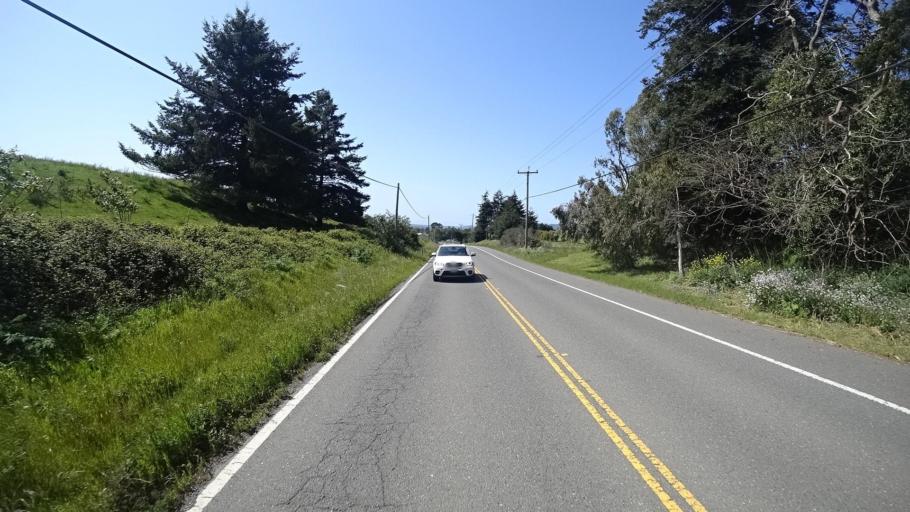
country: US
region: California
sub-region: Humboldt County
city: Hydesville
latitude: 40.5604
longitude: -124.1250
